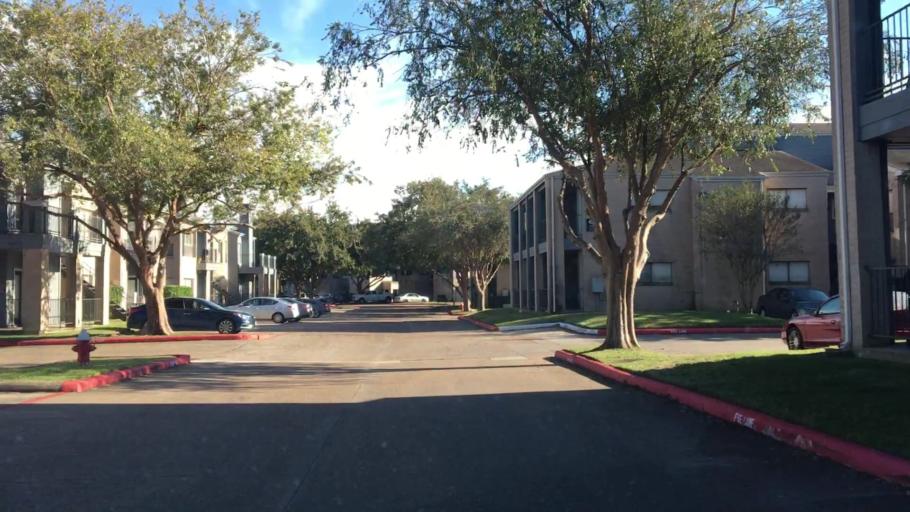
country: US
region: Texas
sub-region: Harris County
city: Nassau Bay
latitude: 29.5362
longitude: -95.1013
